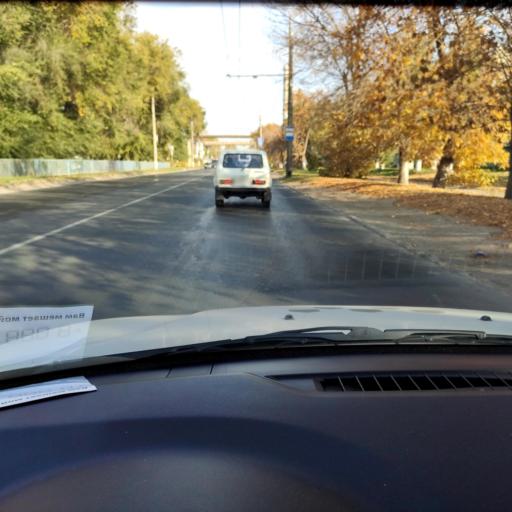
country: RU
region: Samara
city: Tol'yatti
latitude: 53.5428
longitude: 49.4446
